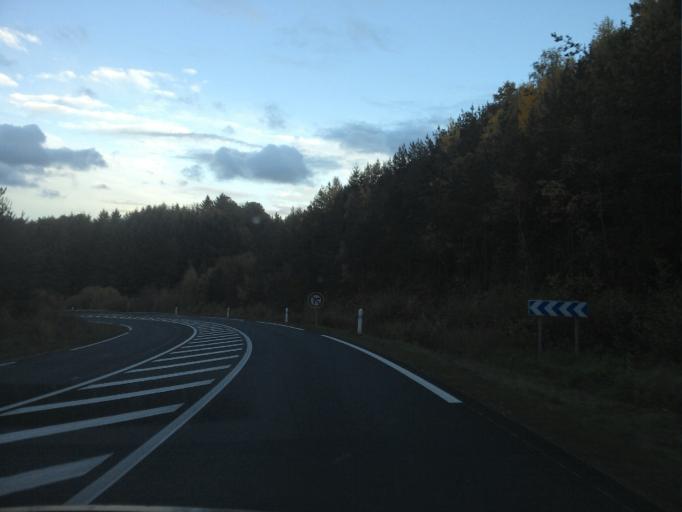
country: FR
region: Auvergne
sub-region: Departement du Puy-de-Dome
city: Saint-Ours
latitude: 45.8335
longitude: 2.8323
